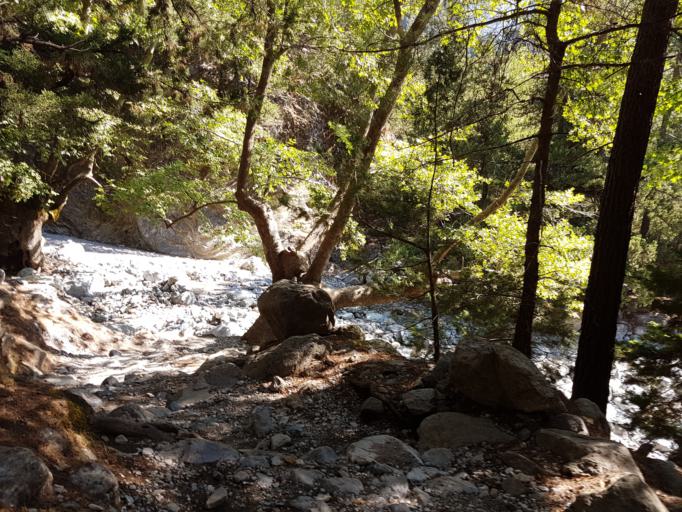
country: GR
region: Crete
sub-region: Nomos Chanias
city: Perivolia
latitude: 35.3070
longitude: 23.9335
